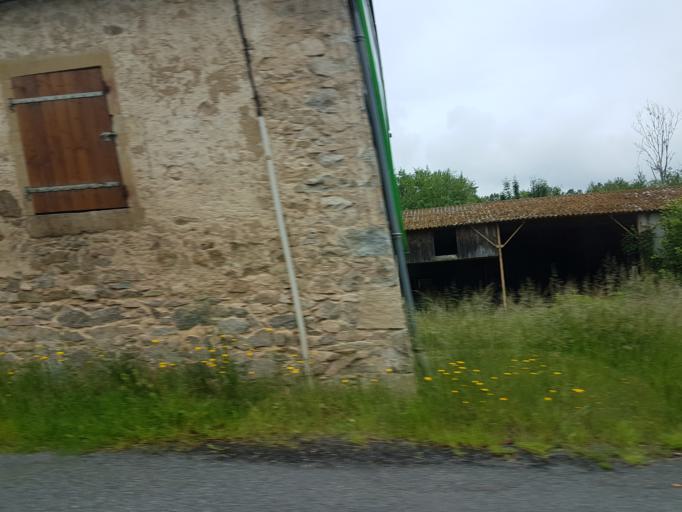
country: FR
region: Bourgogne
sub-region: Departement de la Nievre
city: Chateau-Chinon(Ville)
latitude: 47.0486
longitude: 3.9666
